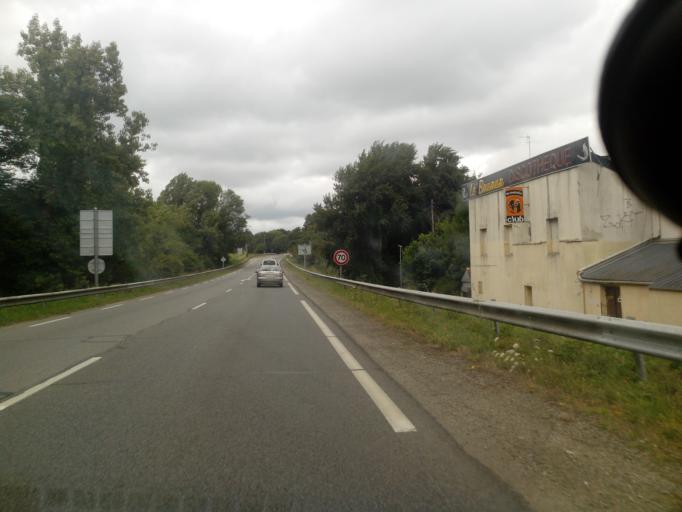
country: FR
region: Brittany
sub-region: Departement du Morbihan
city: Hennebont
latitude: 47.7831
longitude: -3.2757
